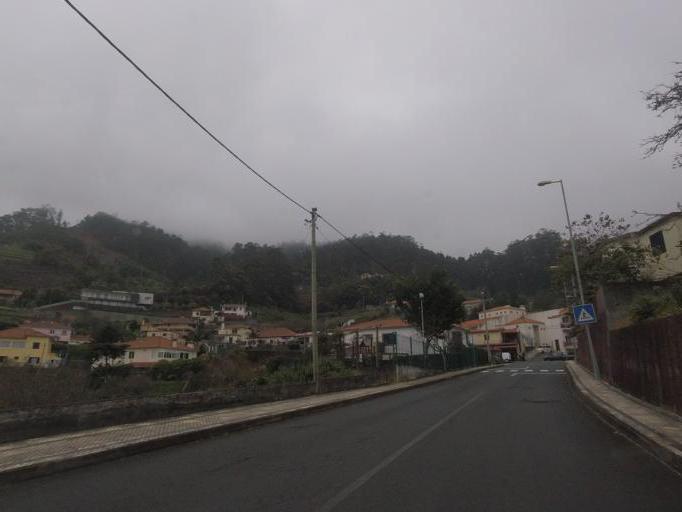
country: PT
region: Madeira
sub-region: Santa Cruz
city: Santa Cruz
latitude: 32.7347
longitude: -16.8198
